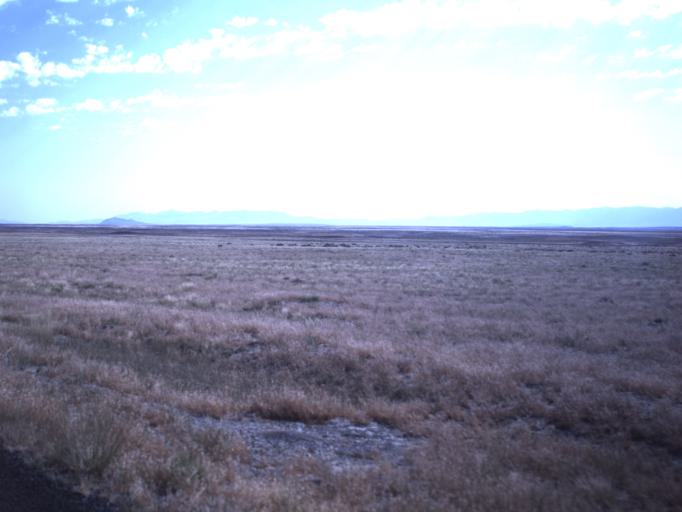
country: US
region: Utah
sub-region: Beaver County
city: Milford
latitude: 38.8495
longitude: -112.8426
